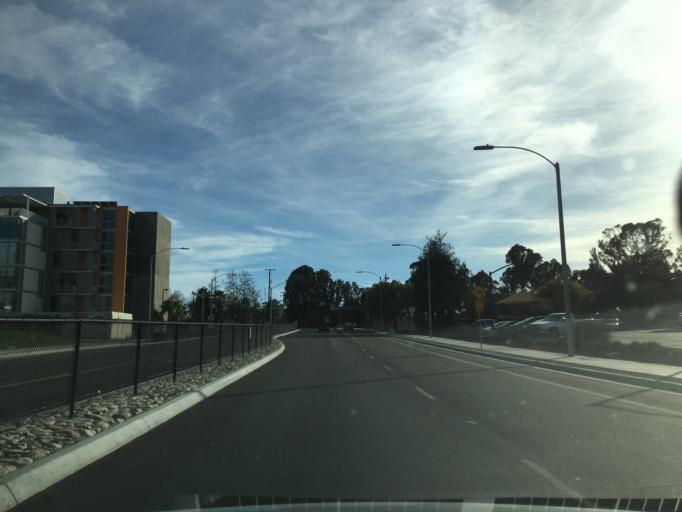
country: US
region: California
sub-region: Santa Barbara County
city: Isla Vista
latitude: 34.4188
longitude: -119.8698
